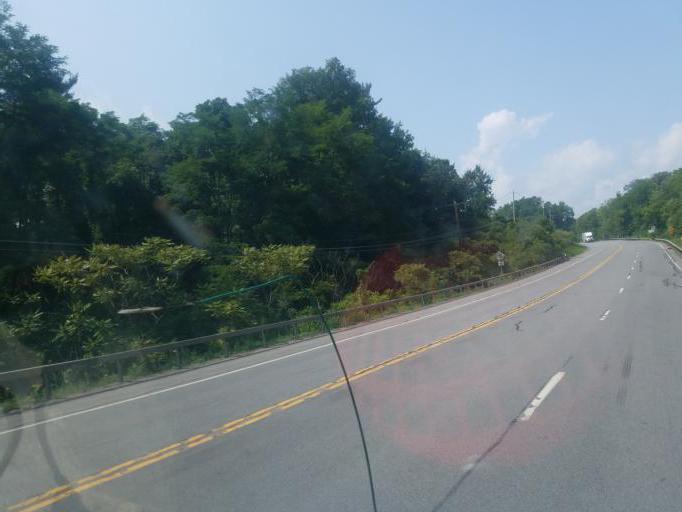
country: US
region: New York
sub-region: Montgomery County
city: Fonda
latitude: 42.9682
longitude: -74.3885
